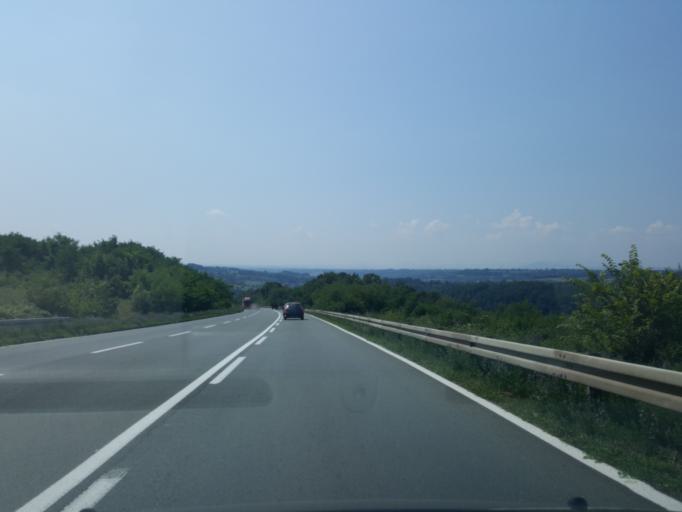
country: RS
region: Central Serbia
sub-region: Belgrade
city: Sopot
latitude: 44.5124
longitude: 20.6530
